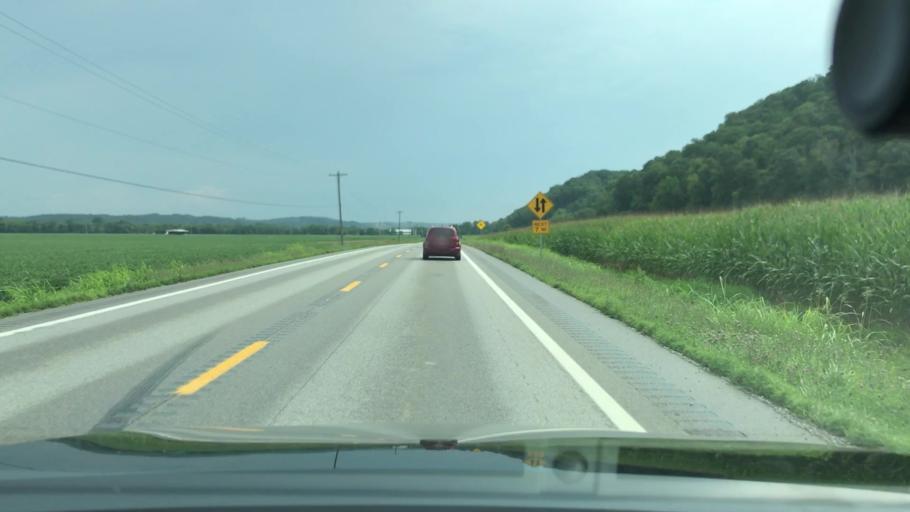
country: US
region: West Virginia
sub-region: Putnam County
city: Buffalo
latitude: 38.6705
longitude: -81.9668
